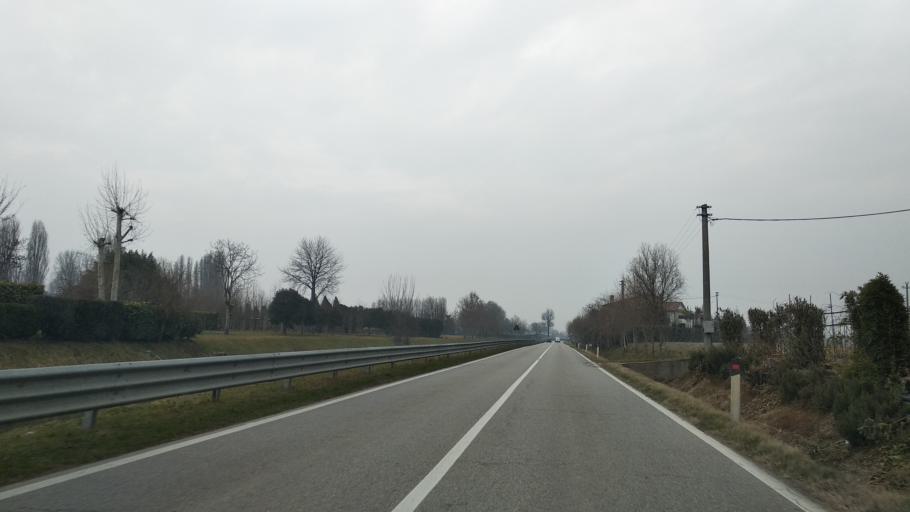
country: IT
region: Veneto
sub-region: Provincia di Padova
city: Villa del Conte
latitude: 45.5592
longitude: 11.8696
